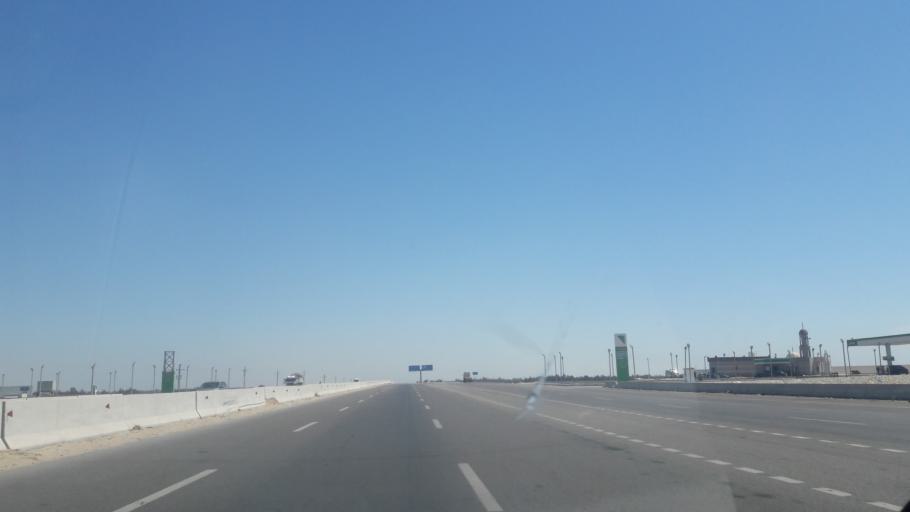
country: EG
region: Al Isma'iliyah
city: Ismailia
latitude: 30.8410
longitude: 32.1665
